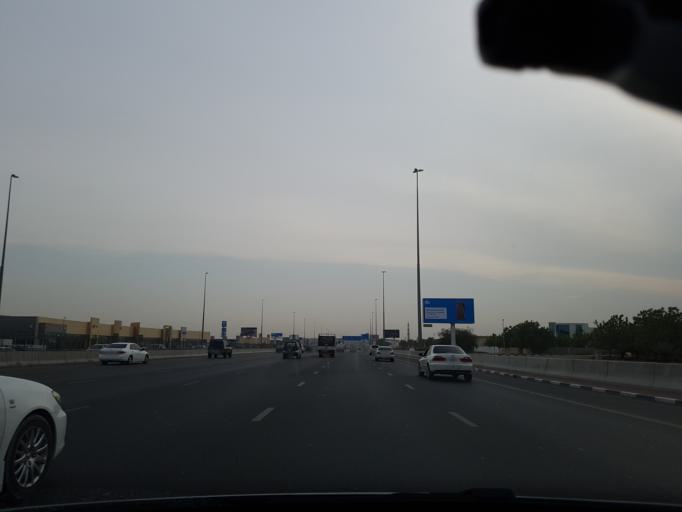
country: AE
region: Ash Shariqah
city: Sharjah
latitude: 25.3497
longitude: 55.4761
